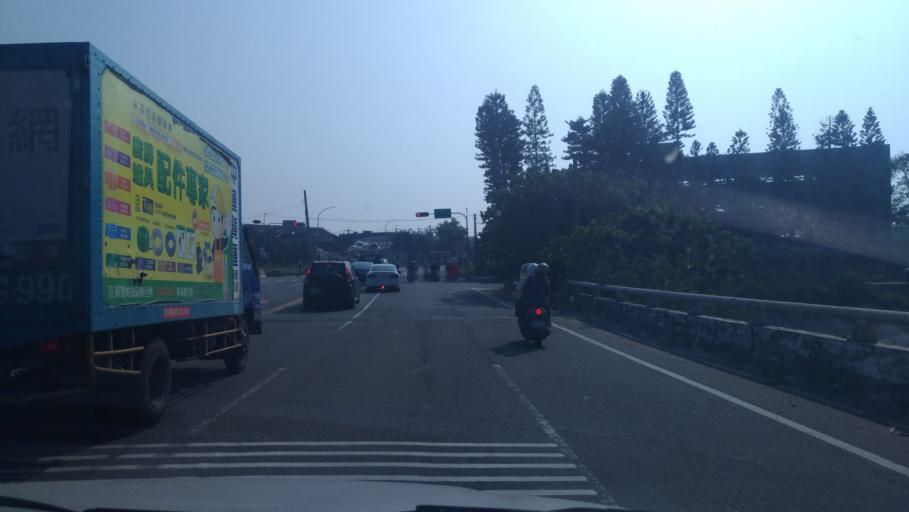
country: TW
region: Taiwan
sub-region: Chiayi
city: Jiayi Shi
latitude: 23.5092
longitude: 120.4348
